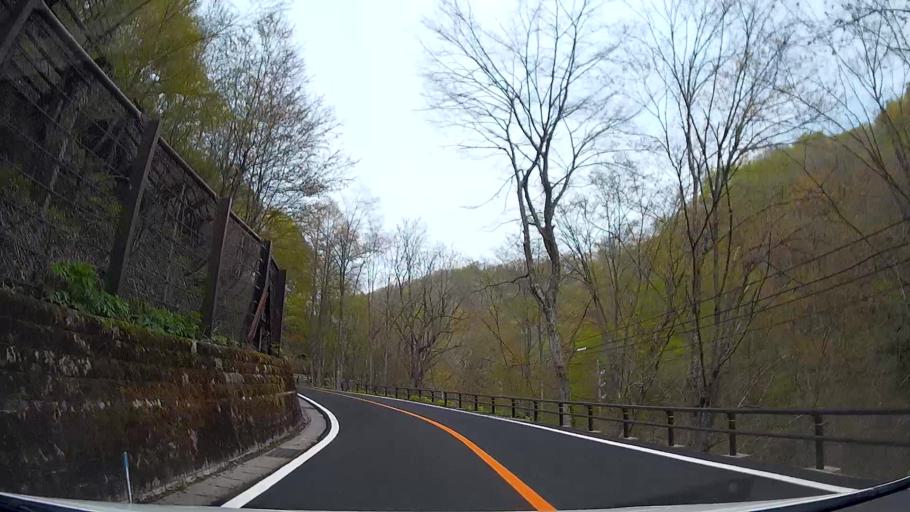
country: JP
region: Akita
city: Hanawa
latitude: 40.3863
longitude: 140.8849
